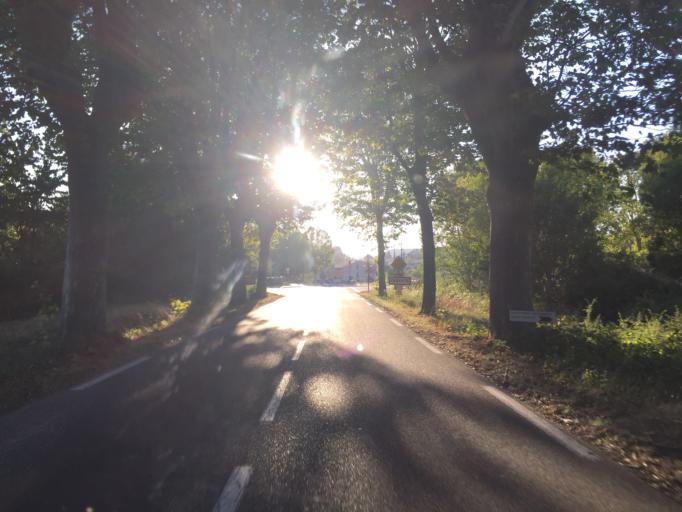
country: FR
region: Provence-Alpes-Cote d'Azur
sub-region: Departement des Alpes-de-Haute-Provence
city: Cereste
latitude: 43.8575
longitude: 5.6000
